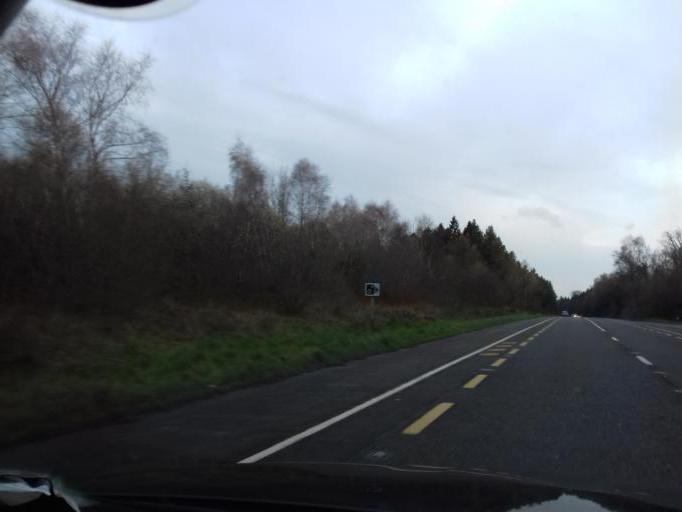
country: IE
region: Leinster
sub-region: Laois
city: Abbeyleix
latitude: 52.8906
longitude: -7.3636
